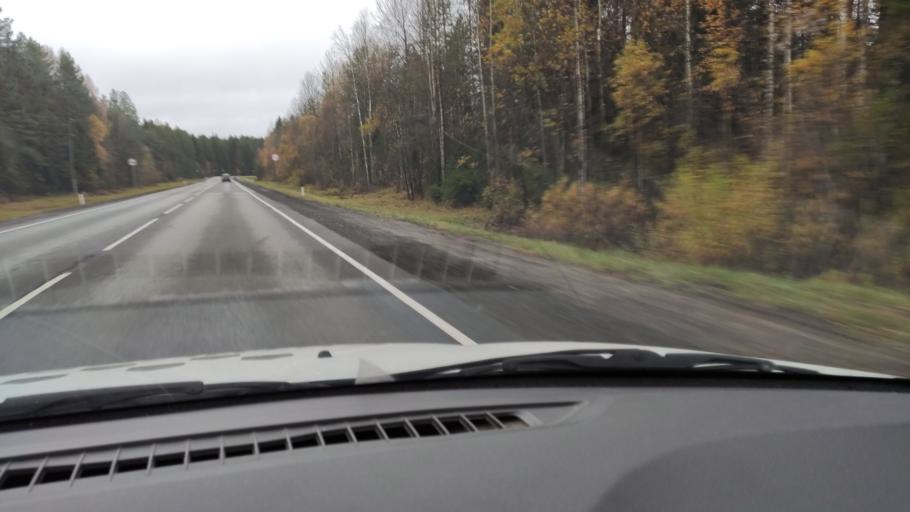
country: RU
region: Kirov
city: Belaya Kholunitsa
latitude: 58.8810
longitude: 50.8717
